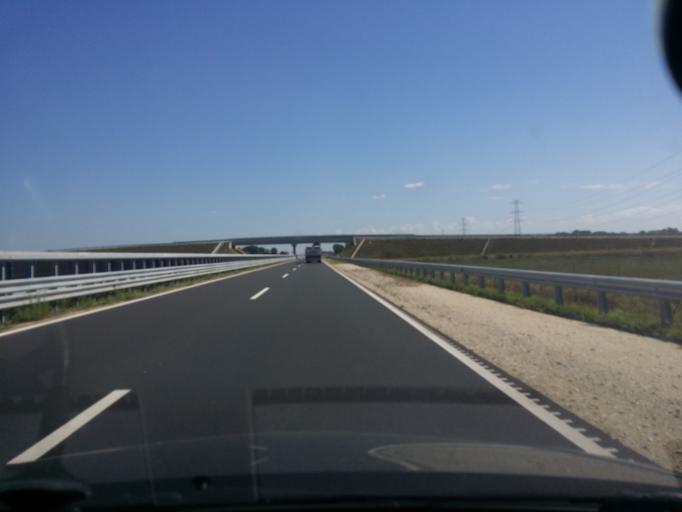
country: HU
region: Vas
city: Repcelak
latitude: 47.3789
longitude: 16.9584
